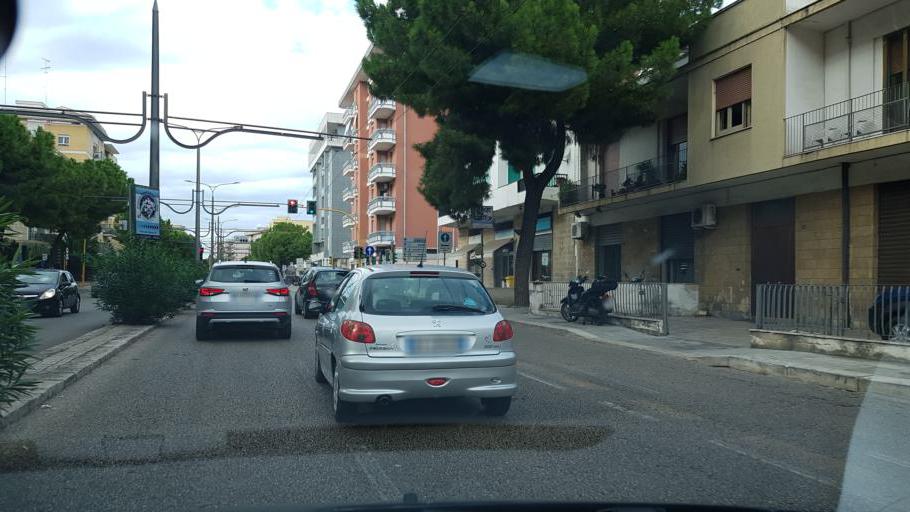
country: IT
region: Apulia
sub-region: Provincia di Lecce
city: Lecce
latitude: 40.3546
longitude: 18.1852
